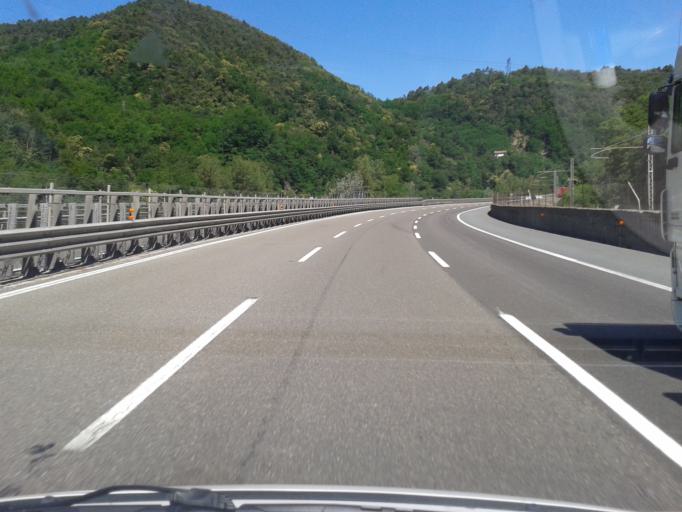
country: IT
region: Piedmont
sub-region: Provincia di Alessandria
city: Belforte Monferrato
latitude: 44.6026
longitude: 8.6643
